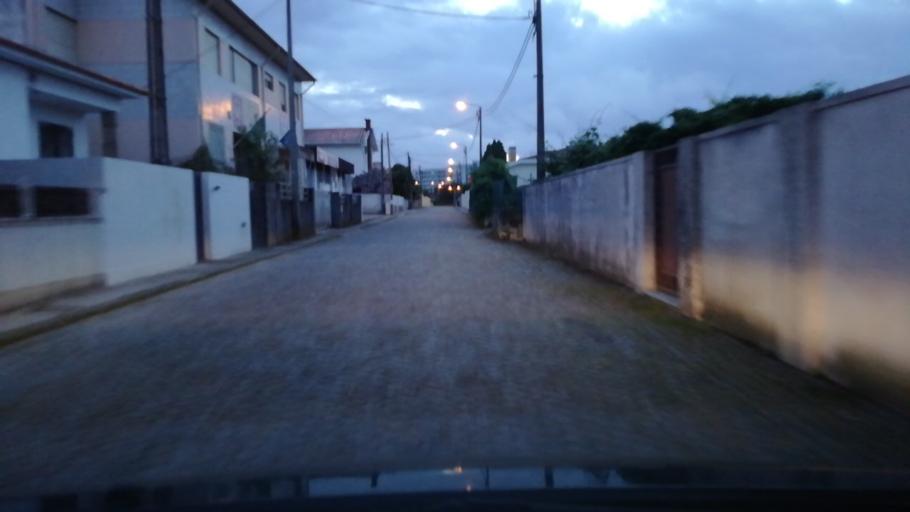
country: PT
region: Porto
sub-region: Maia
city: Anta
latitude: 41.2621
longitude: -8.6083
